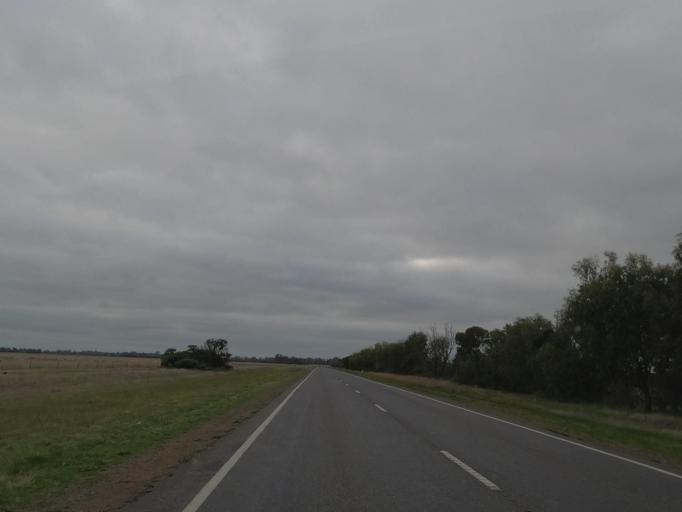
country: AU
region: Victoria
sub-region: Greater Bendigo
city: Long Gully
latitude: -36.4608
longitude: 143.9648
